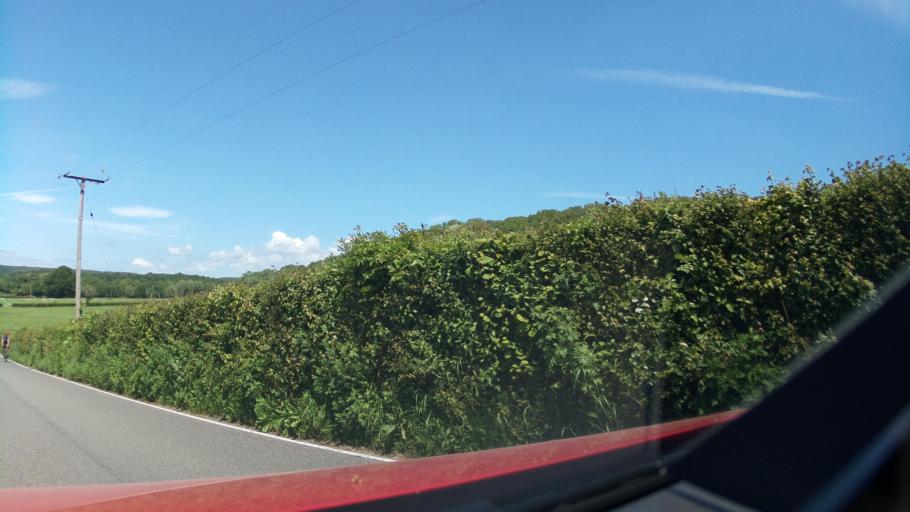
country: GB
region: Wales
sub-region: Monmouthshire
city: Caldicot
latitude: 51.6003
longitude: -2.7367
